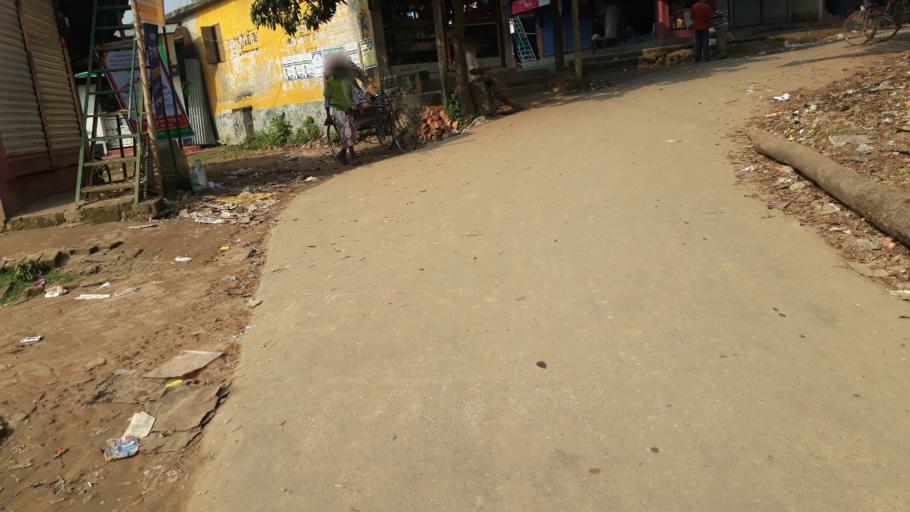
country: BD
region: Dhaka
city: Tungi
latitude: 23.8831
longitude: 90.2592
